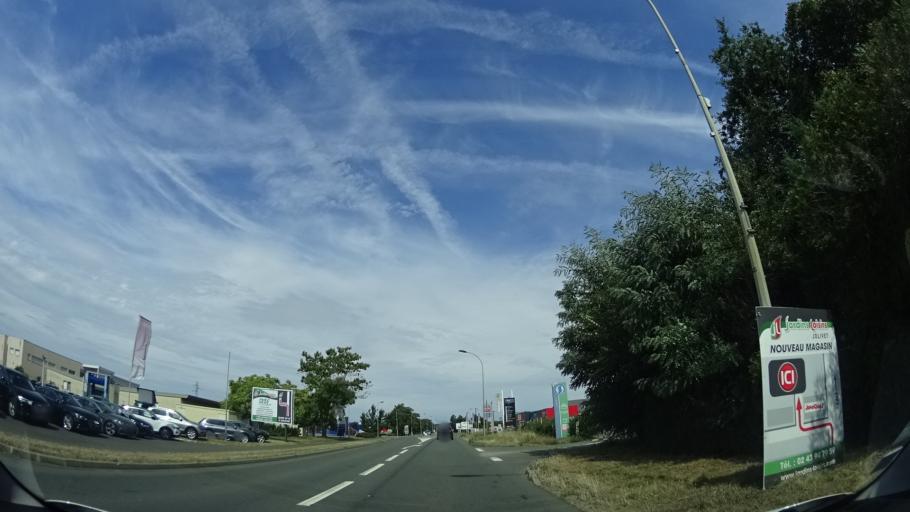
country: FR
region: Pays de la Loire
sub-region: Departement de la Sarthe
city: La Fleche
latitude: 47.7067
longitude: -0.0950
